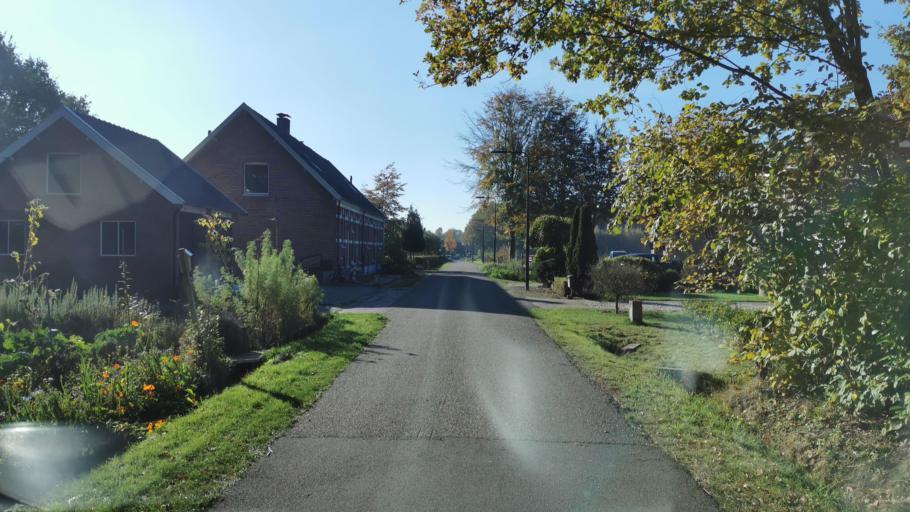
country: NL
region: Overijssel
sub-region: Gemeente Enschede
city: Enschede
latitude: 52.2553
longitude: 6.9142
